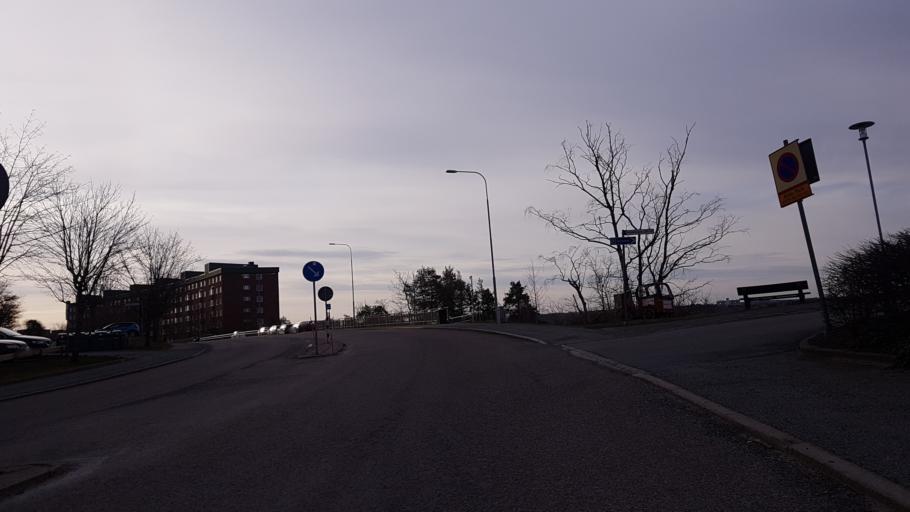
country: SE
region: Stockholm
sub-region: Lidingo
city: Lidingoe
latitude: 59.3480
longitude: 18.1413
